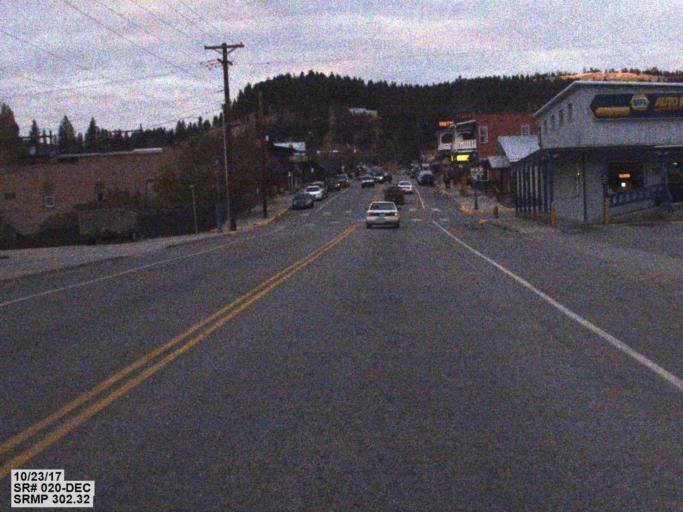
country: US
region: Washington
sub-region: Ferry County
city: Republic
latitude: 48.6442
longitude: -118.7375
